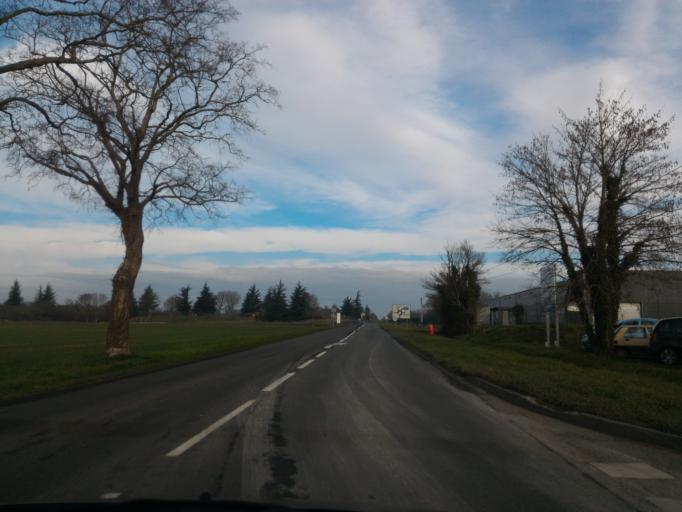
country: FR
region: Poitou-Charentes
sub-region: Departement de la Charente
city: Ruffec
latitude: 46.0438
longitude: 0.1979
